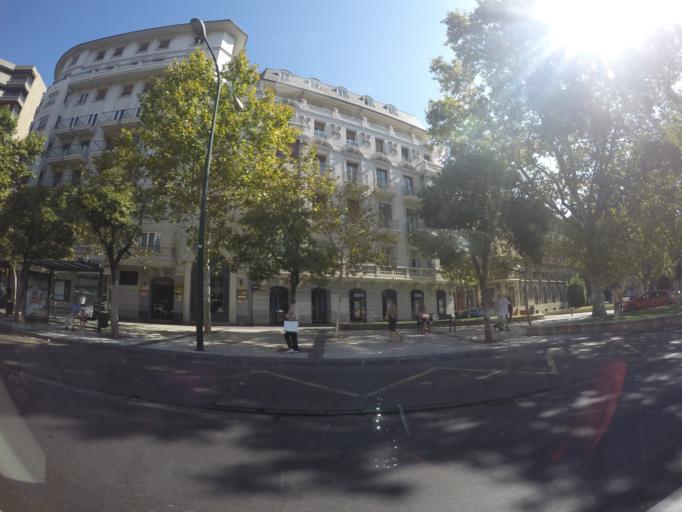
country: ES
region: Aragon
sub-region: Provincia de Zaragoza
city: Zaragoza
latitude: 41.6481
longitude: -0.8866
